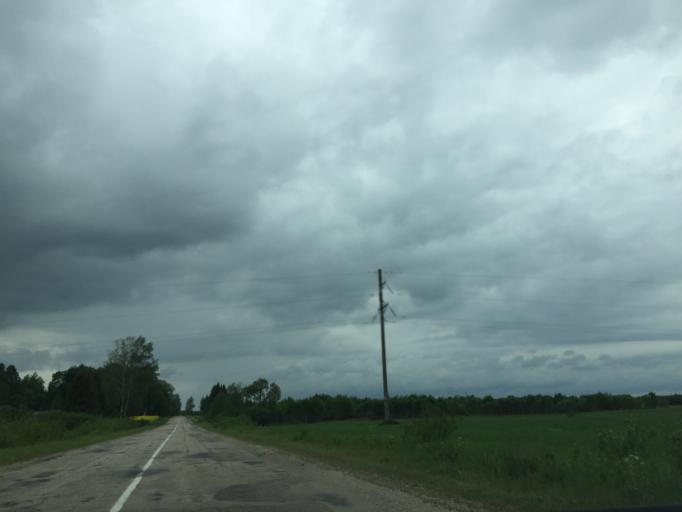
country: LV
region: Varkava
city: Vecvarkava
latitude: 56.0852
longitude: 26.5968
